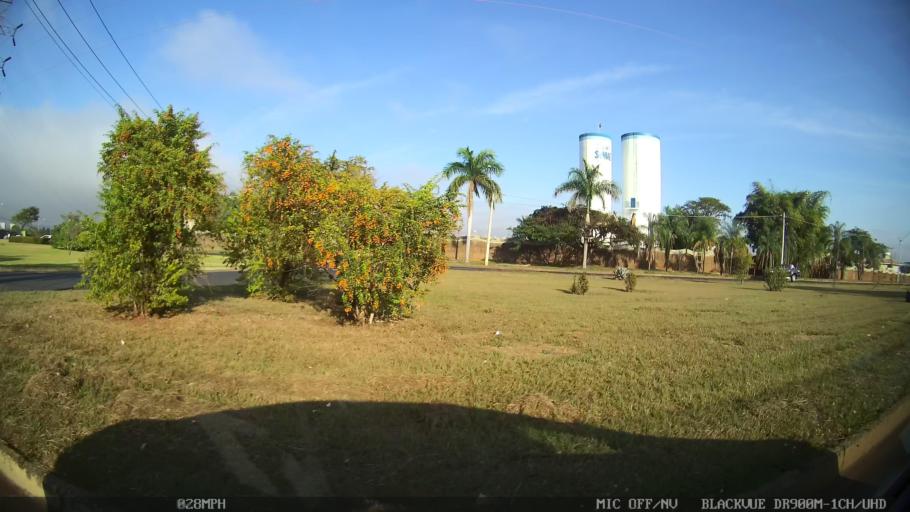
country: BR
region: Sao Paulo
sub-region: Sao Jose Do Rio Preto
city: Sao Jose do Rio Preto
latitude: -20.8157
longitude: -49.3389
